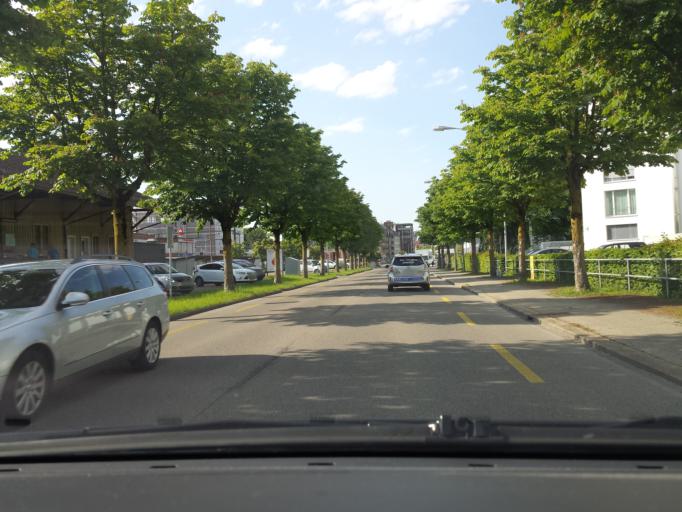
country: CH
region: Thurgau
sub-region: Arbon District
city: Arbon
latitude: 47.5092
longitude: 9.4338
